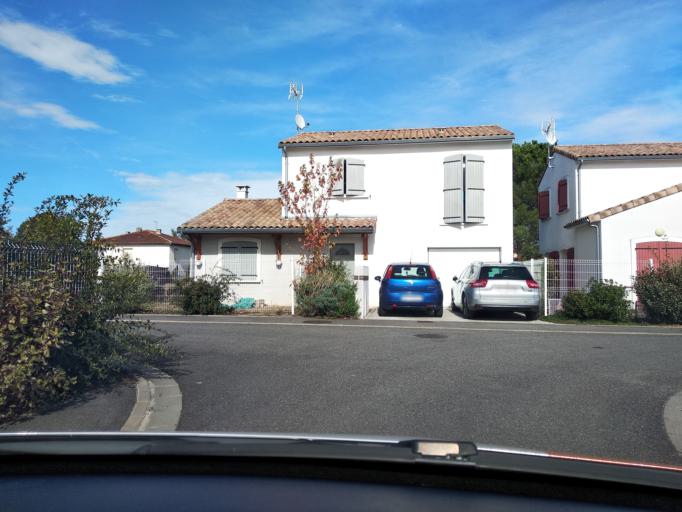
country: FR
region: Midi-Pyrenees
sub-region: Departement du Tarn-et-Garonne
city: Montauban
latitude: 44.0444
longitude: 1.3301
